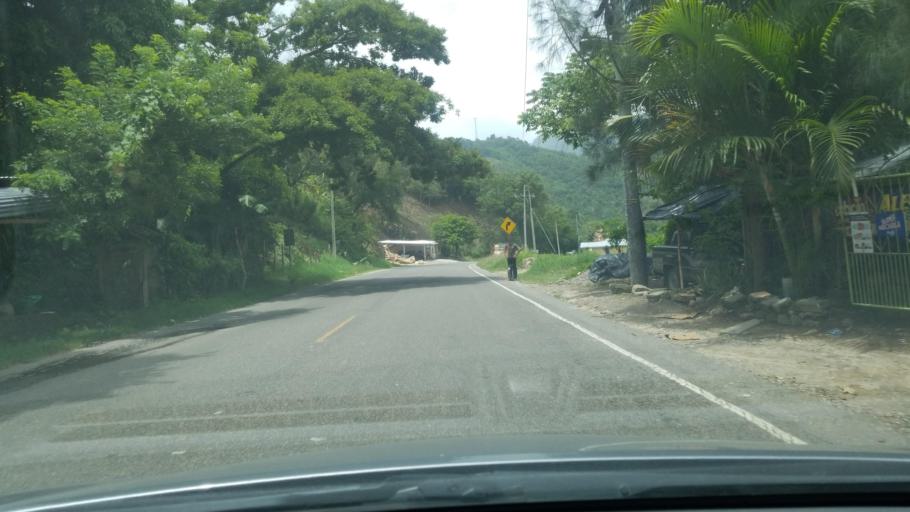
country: HN
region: Copan
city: Ojos de Agua
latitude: 14.6783
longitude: -88.8177
